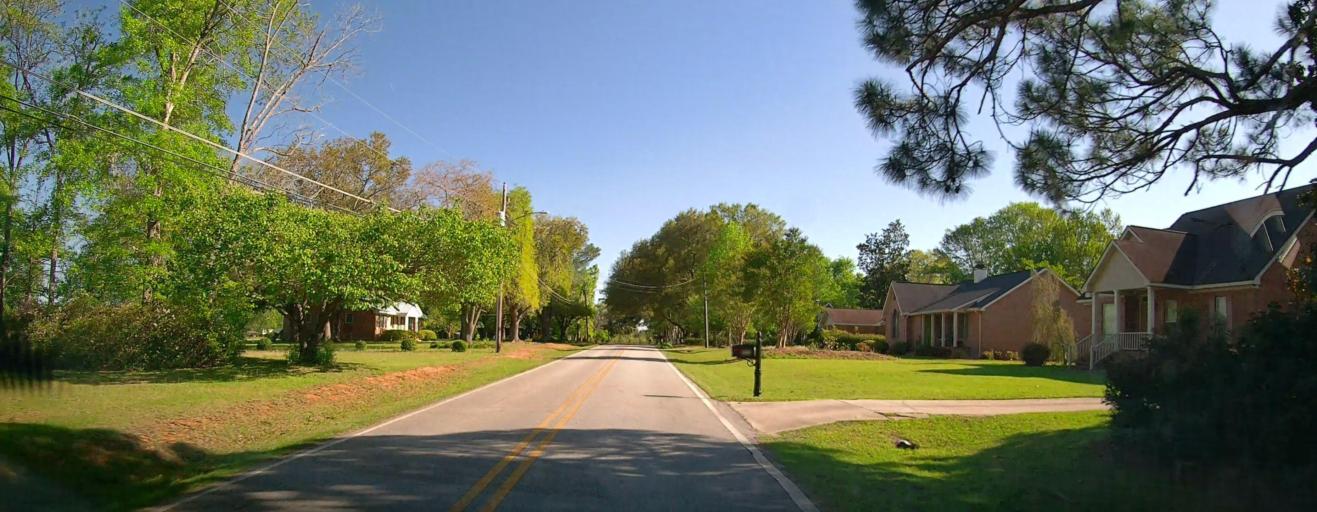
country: US
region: Georgia
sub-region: Houston County
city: Perry
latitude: 32.4531
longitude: -83.7080
